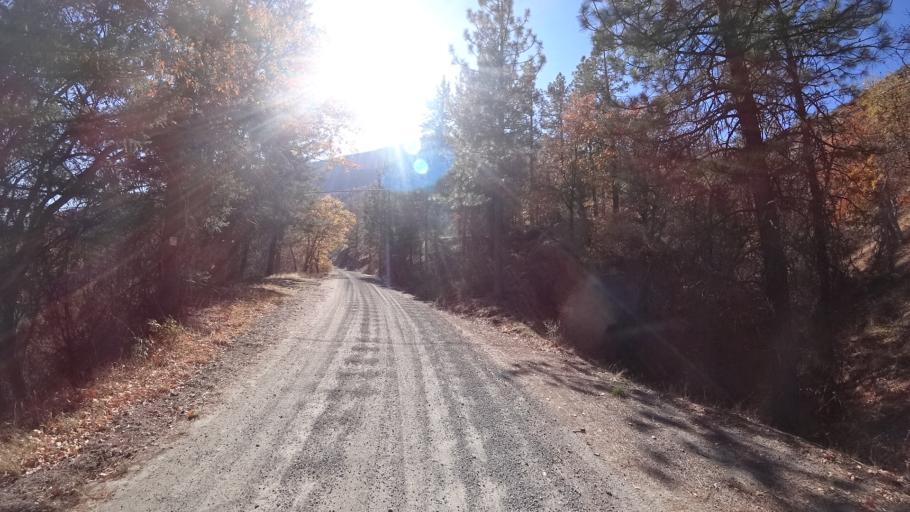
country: US
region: California
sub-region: Siskiyou County
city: Yreka
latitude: 41.8516
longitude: -122.6954
